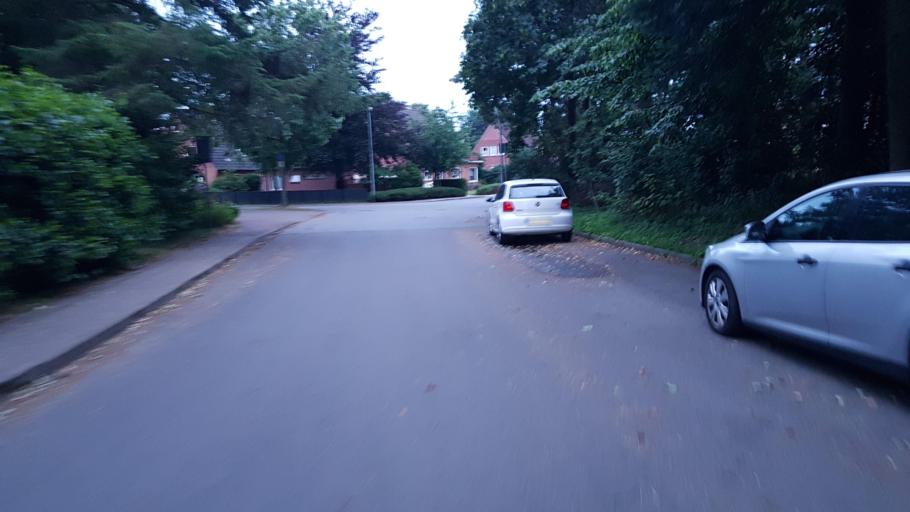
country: DE
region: Schleswig-Holstein
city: Sankt Peter-Ording
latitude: 54.3080
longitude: 8.6260
